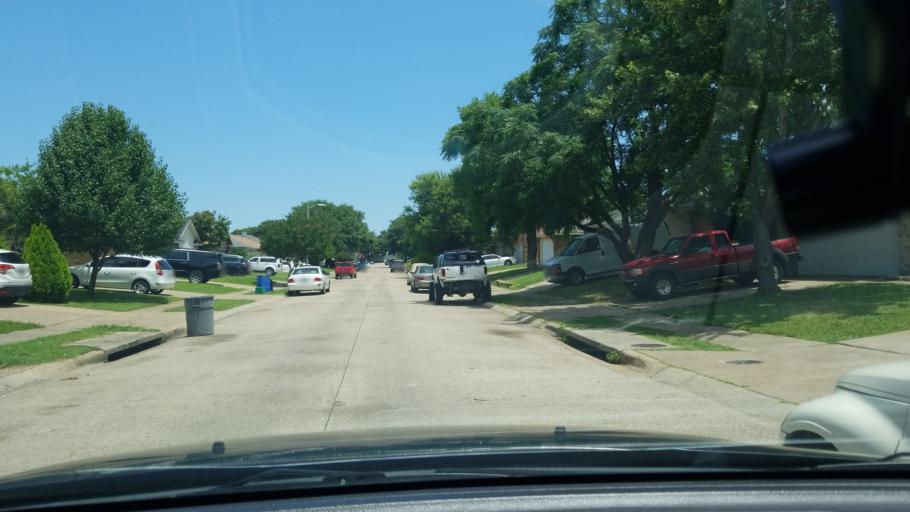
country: US
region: Texas
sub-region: Dallas County
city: Mesquite
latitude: 32.8015
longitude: -96.6601
